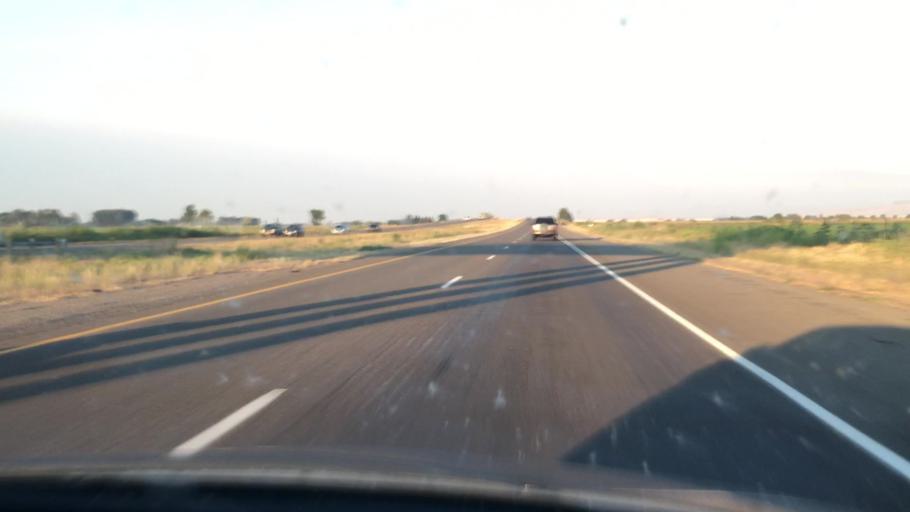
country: US
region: Idaho
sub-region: Minidoka County
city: Rupert
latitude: 42.5687
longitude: -113.6678
